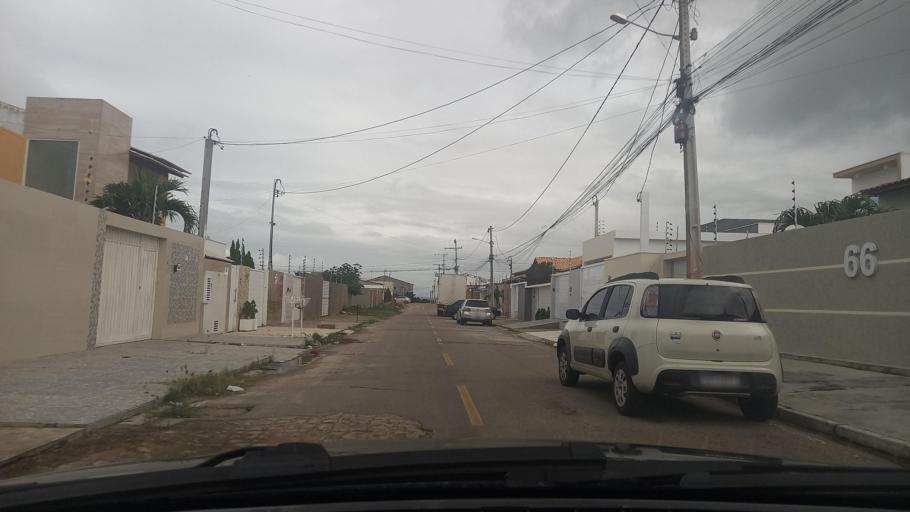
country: BR
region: Bahia
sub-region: Paulo Afonso
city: Paulo Afonso
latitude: -9.3990
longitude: -38.2439
